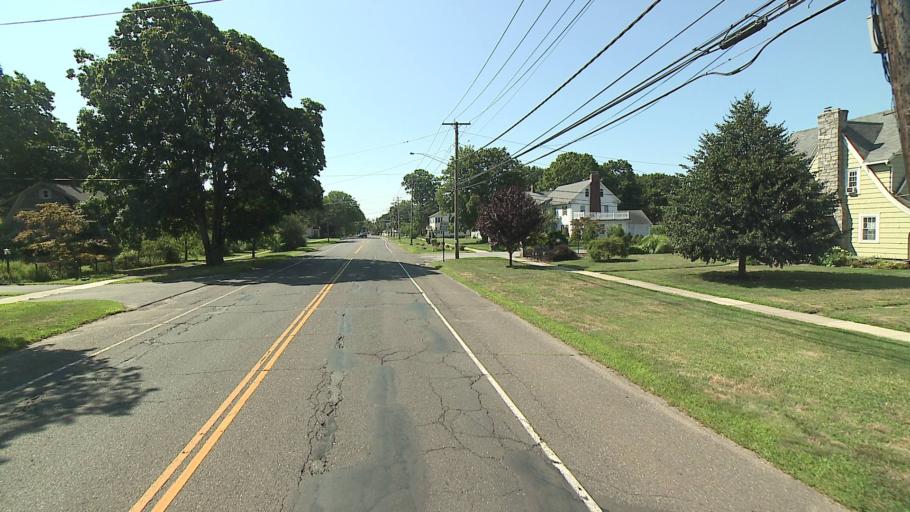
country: US
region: Connecticut
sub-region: Fairfield County
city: Stratford
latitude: 41.1811
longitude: -73.1303
